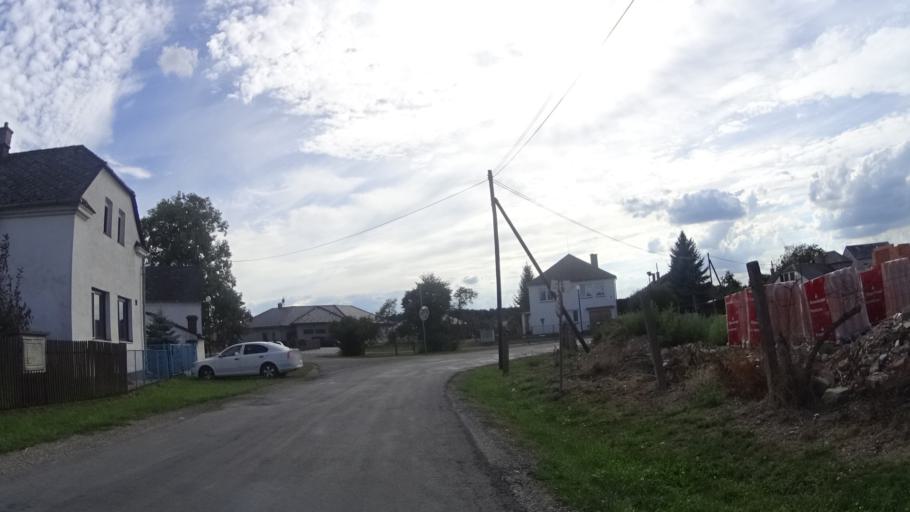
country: CZ
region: Olomoucky
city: Dubicko
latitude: 49.7964
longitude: 16.9620
